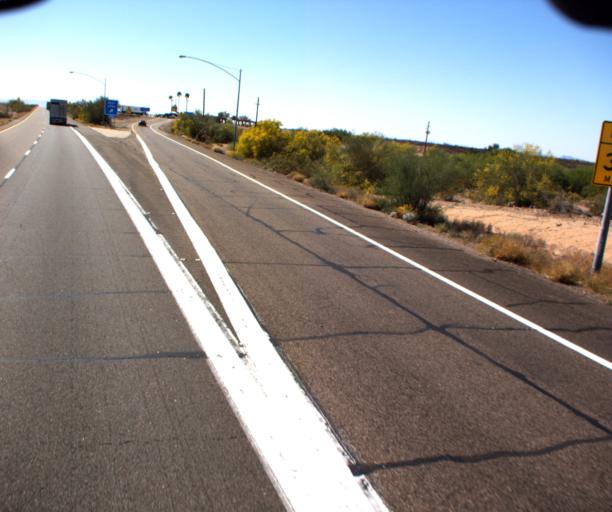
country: US
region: Arizona
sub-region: Maricopa County
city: Gila Bend
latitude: 32.8554
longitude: -113.2492
